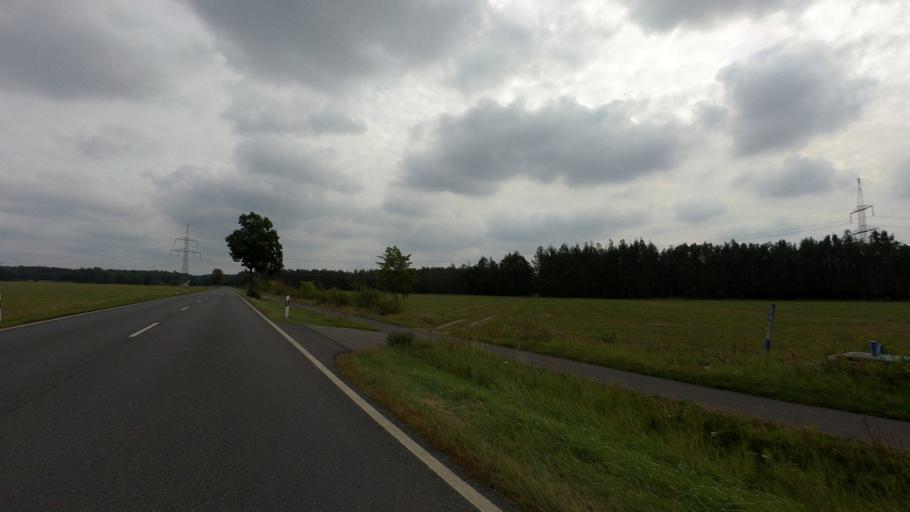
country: DE
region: Brandenburg
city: Sonnewalde
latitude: 51.6618
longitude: 13.6515
